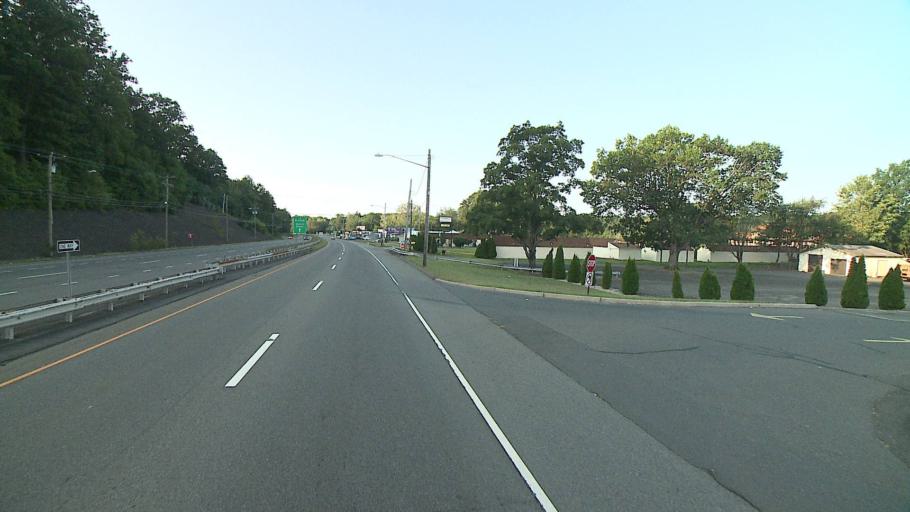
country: US
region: Connecticut
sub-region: New Haven County
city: Meriden
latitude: 41.5646
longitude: -72.7747
